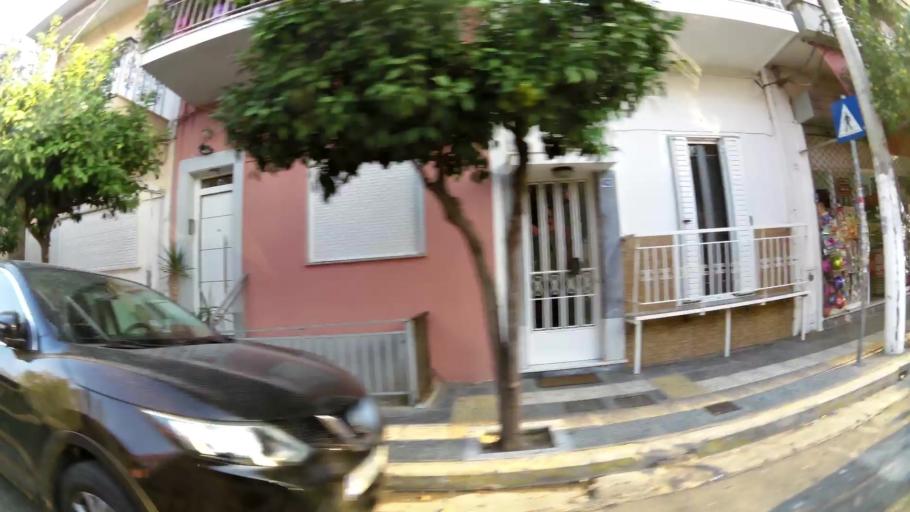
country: GR
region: Attica
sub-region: Nomos Piraios
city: Nikaia
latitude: 37.9677
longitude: 23.6474
